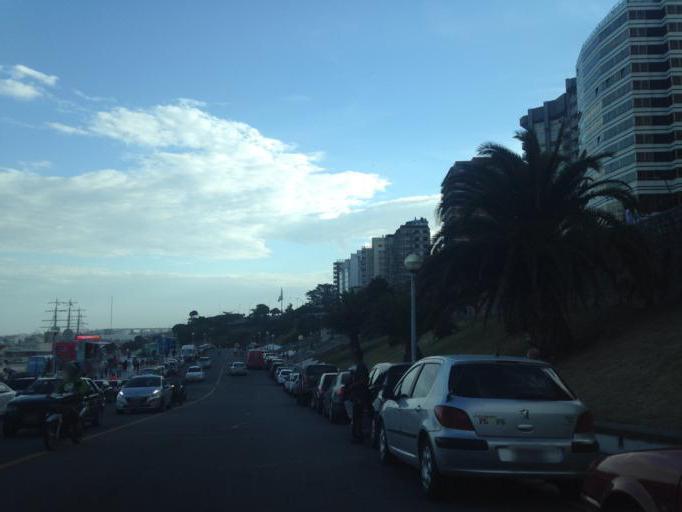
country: AR
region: Buenos Aires
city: Mar del Plata
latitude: -38.0270
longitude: -57.5327
